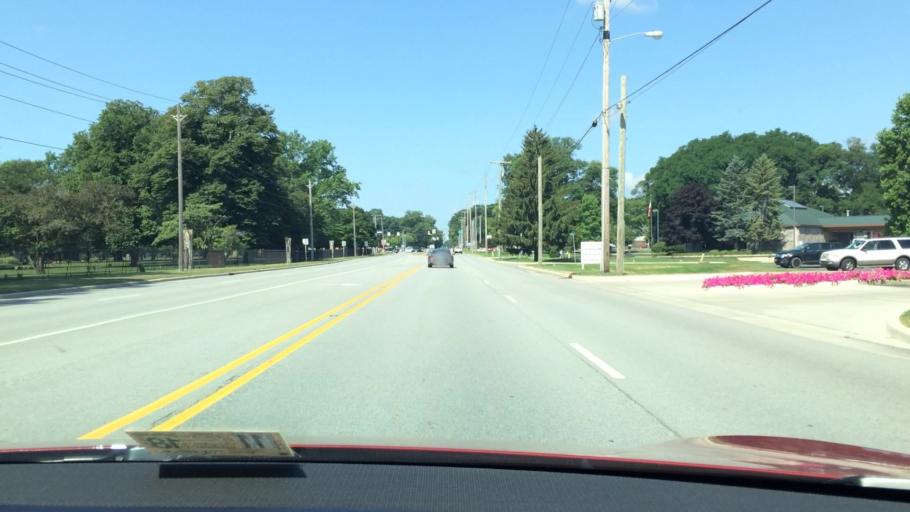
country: US
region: Indiana
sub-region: Saint Joseph County
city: Georgetown
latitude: 41.7239
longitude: -86.1844
